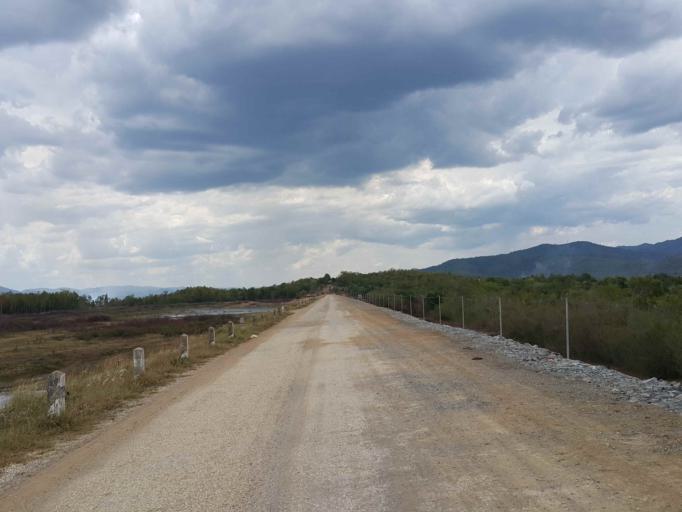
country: TH
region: Sukhothai
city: Thung Saliam
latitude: 17.3184
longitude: 99.4239
